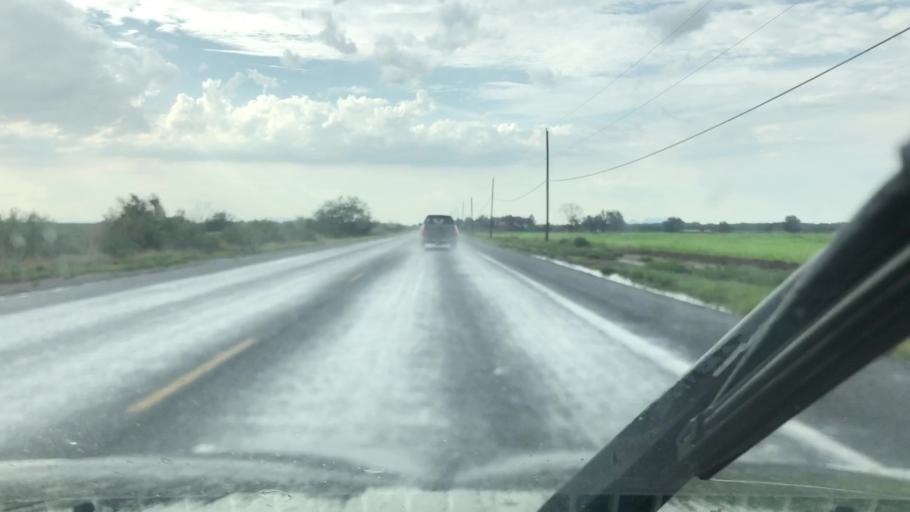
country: US
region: New Mexico
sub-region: Dona Ana County
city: Mesquite
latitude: 32.1835
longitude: -106.7085
